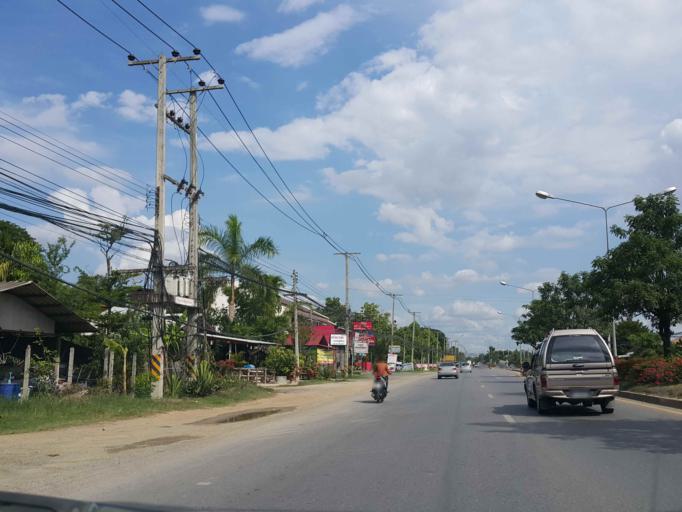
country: TH
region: Chiang Mai
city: San Sai
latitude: 18.9153
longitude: 98.9981
